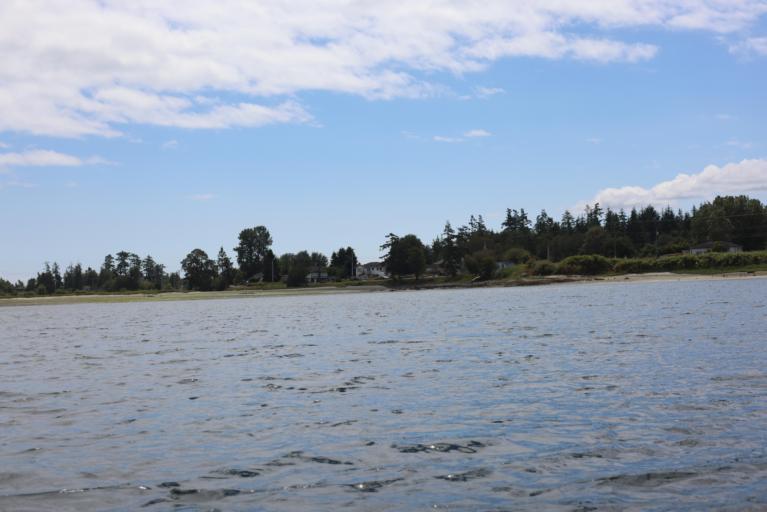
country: CA
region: British Columbia
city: North Saanich
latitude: 48.5939
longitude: -123.3799
